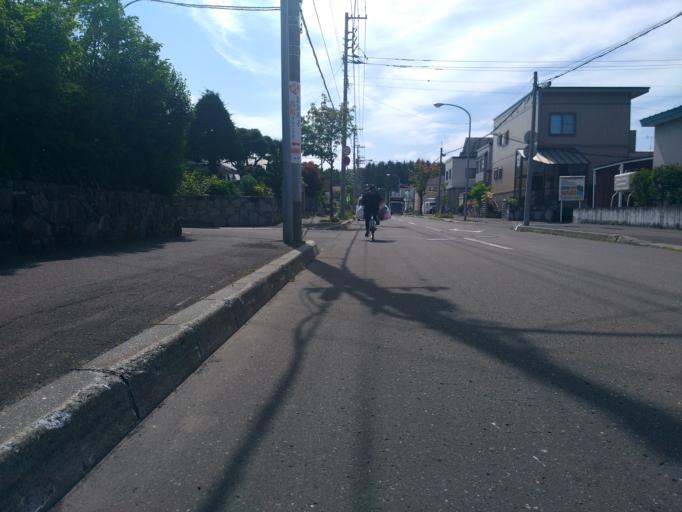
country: JP
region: Hokkaido
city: Ebetsu
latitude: 43.0765
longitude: 141.5003
